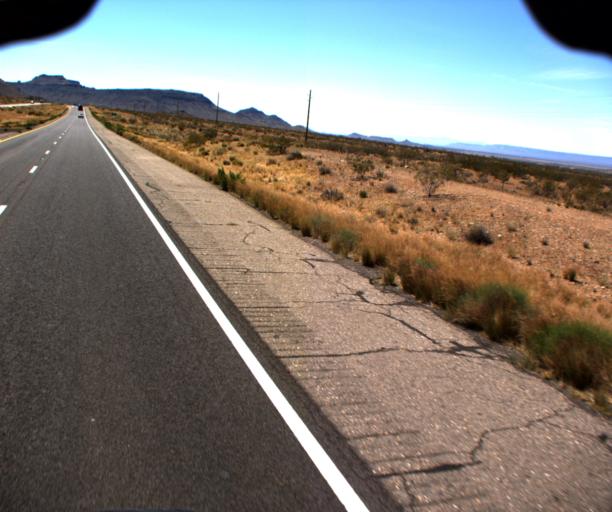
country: US
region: Arizona
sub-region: Mohave County
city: Golden Valley
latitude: 35.2559
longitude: -114.1575
